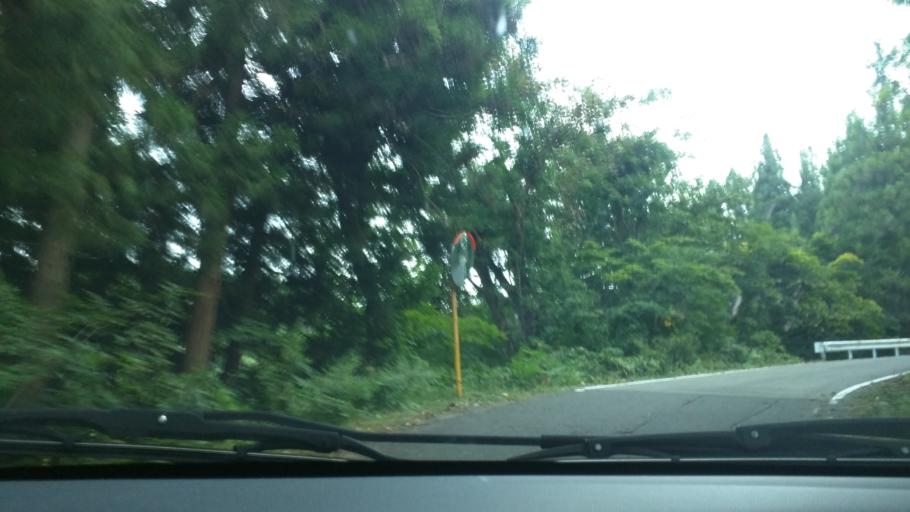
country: JP
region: Fukushima
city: Kitakata
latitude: 37.4483
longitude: 139.6935
